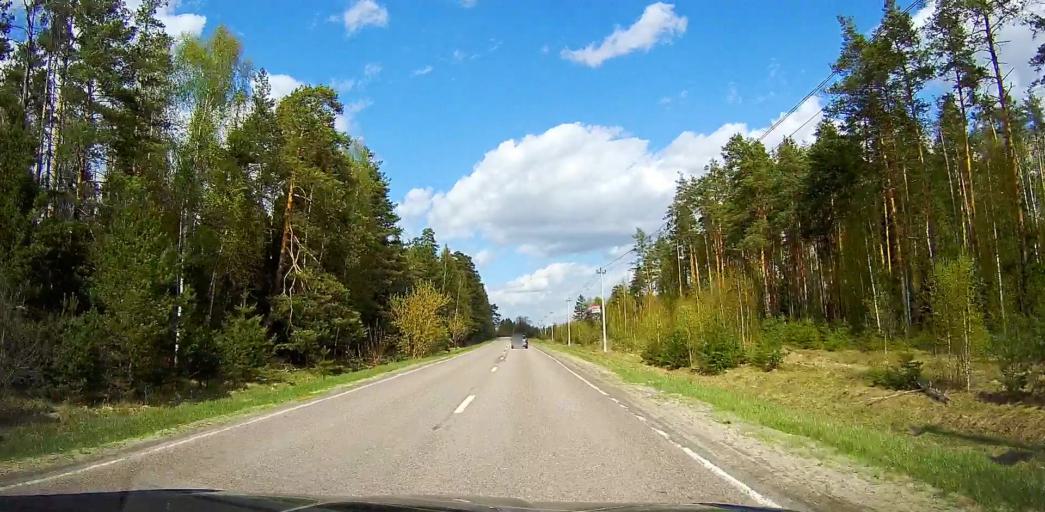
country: RU
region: Moskovskaya
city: Davydovo
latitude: 55.5955
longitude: 38.8376
